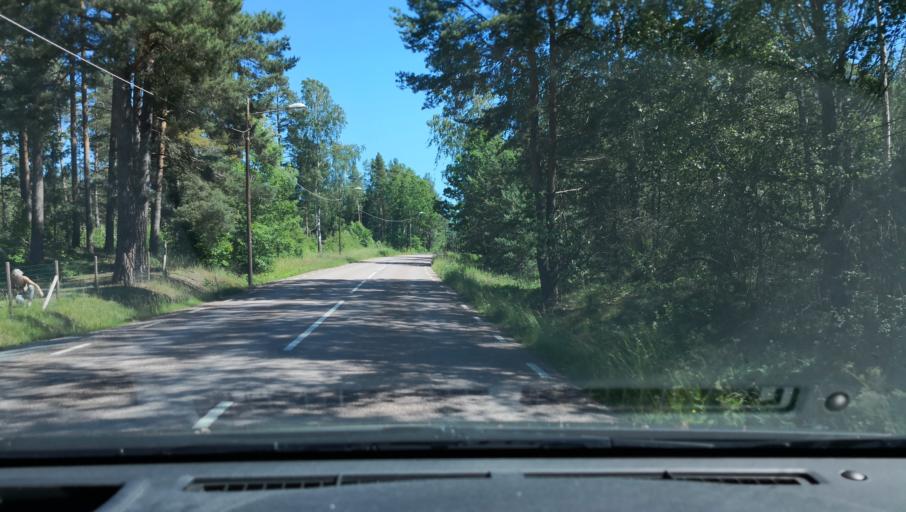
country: SE
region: Vaestmanland
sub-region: Kungsors Kommun
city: Kungsoer
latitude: 59.2916
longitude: 16.0532
